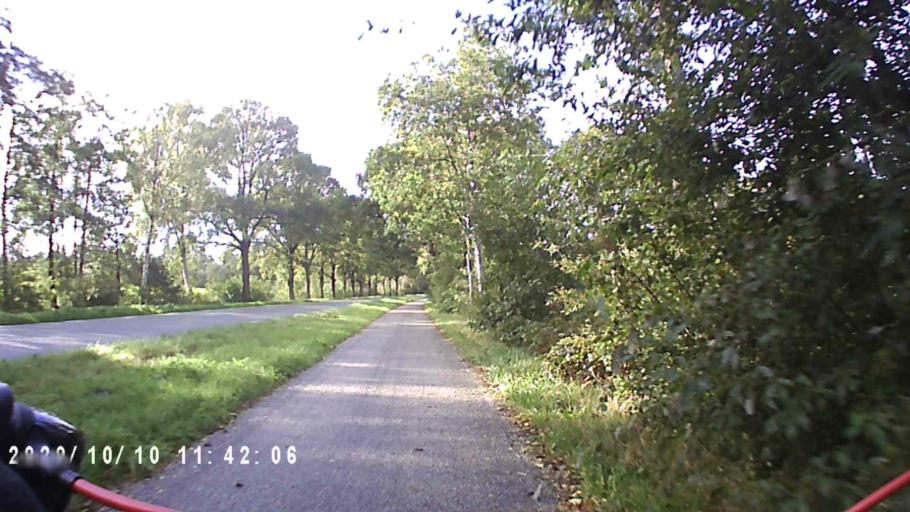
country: NL
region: Friesland
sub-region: Gemeente Smallingerland
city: Drachten
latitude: 53.0630
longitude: 6.0991
